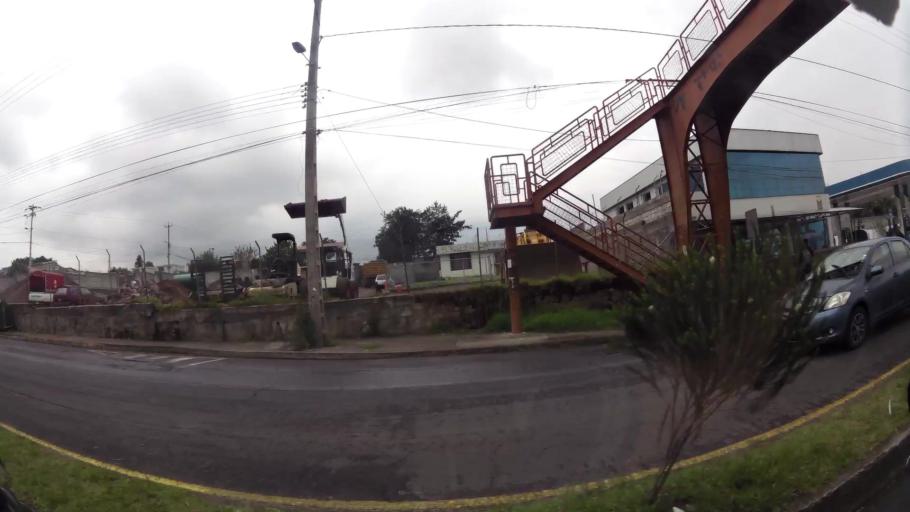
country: EC
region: Pichincha
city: Sangolqui
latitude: -0.3249
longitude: -78.4403
